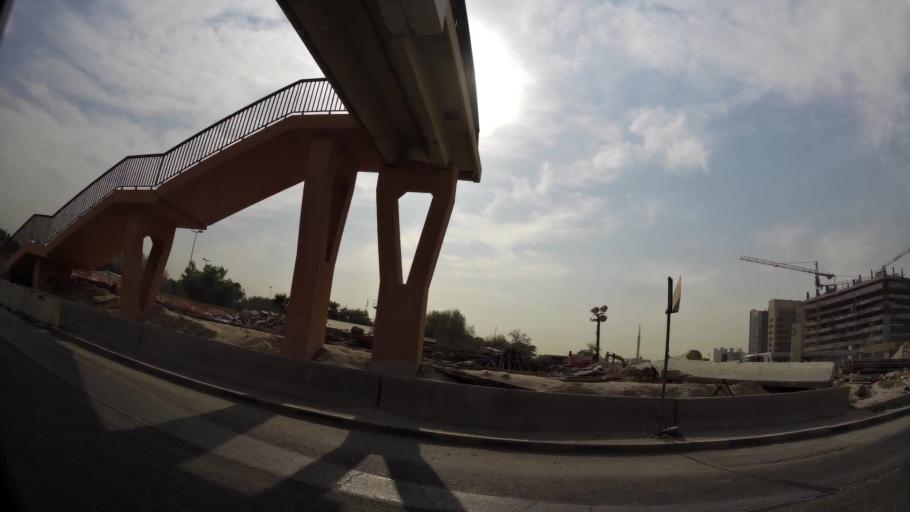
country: KW
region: Al Asimah
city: Ash Shamiyah
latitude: 29.3515
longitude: 47.9446
